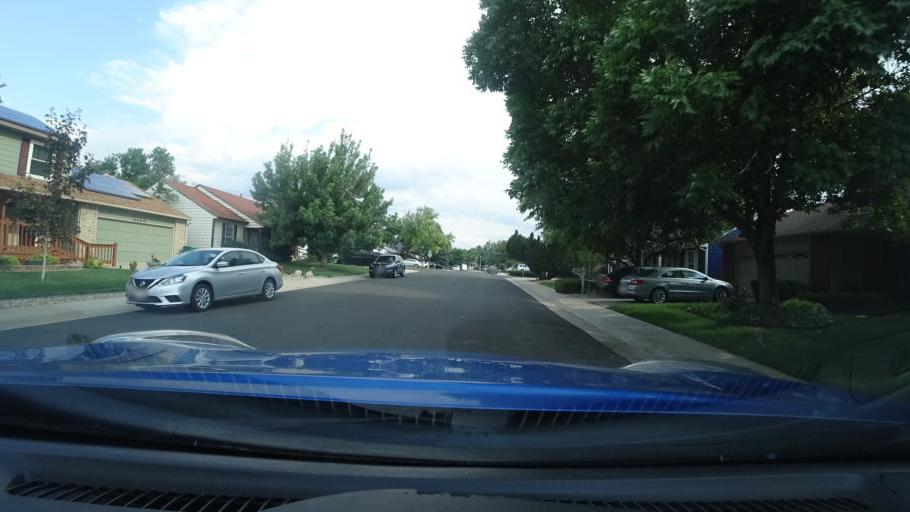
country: US
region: Colorado
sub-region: Adams County
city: Aurora
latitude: 39.6963
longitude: -104.8020
